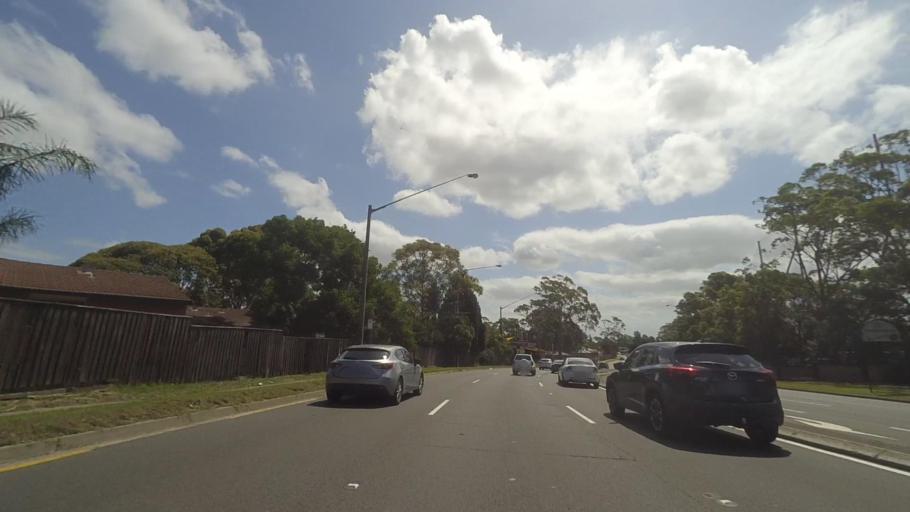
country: AU
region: New South Wales
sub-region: Ku-ring-gai
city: Normanhurst
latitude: -33.7247
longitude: 151.0893
